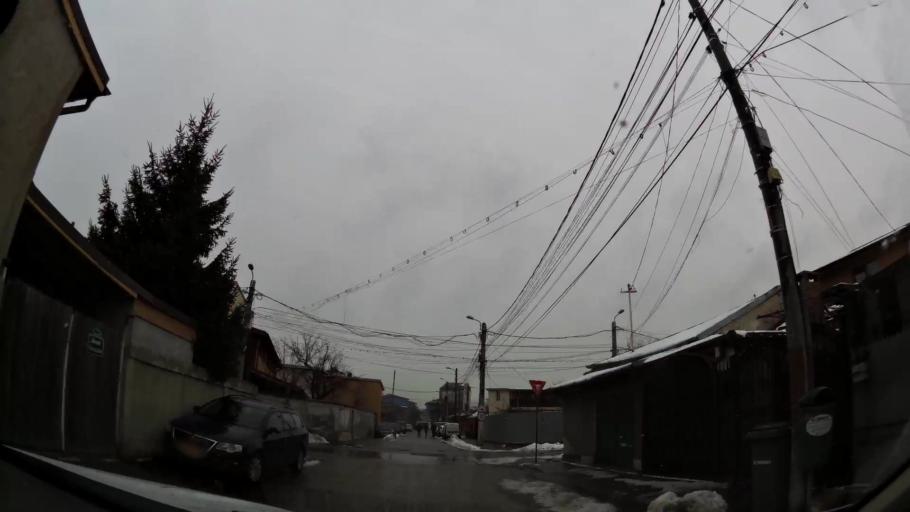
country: RO
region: Ilfov
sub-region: Comuna Mogosoaia
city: Mogosoaia
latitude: 44.4948
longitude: 26.0276
